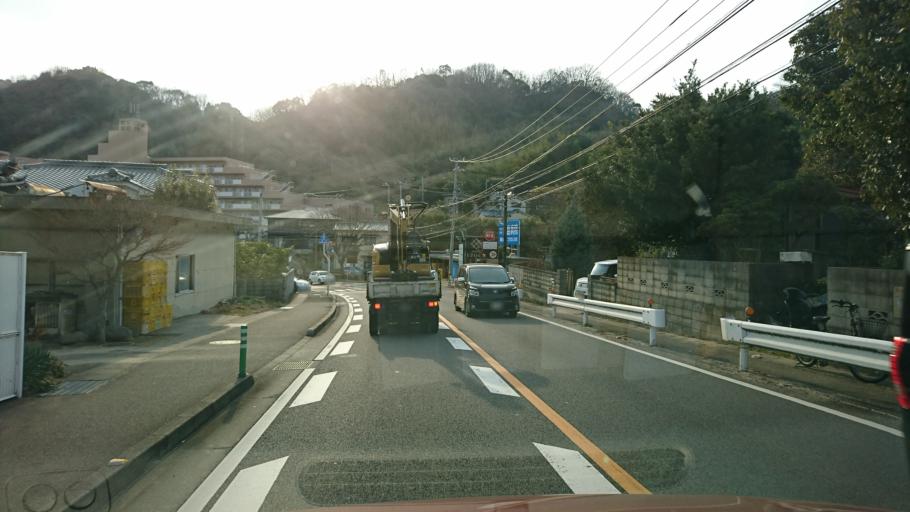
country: JP
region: Ehime
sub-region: Shikoku-chuo Shi
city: Matsuyama
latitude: 33.8653
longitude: 132.7739
